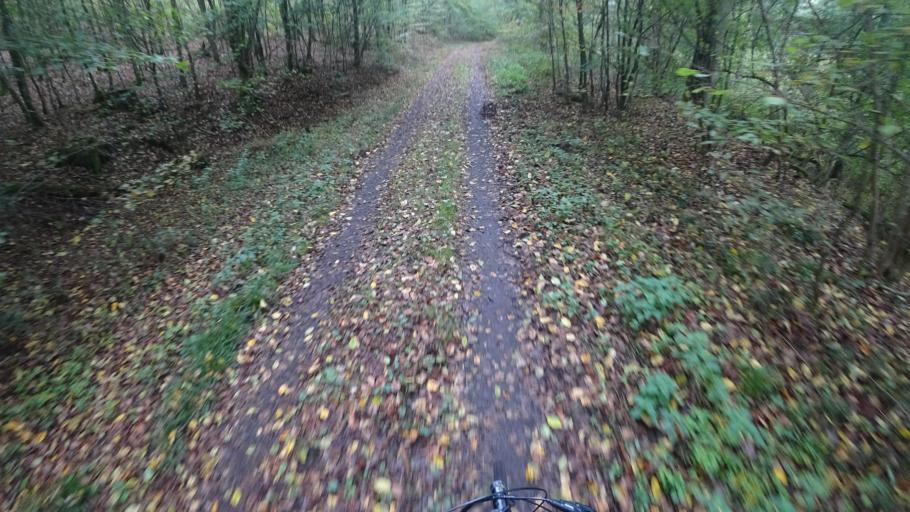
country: DE
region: Rheinland-Pfalz
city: Isselbach
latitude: 50.3992
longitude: 7.8978
